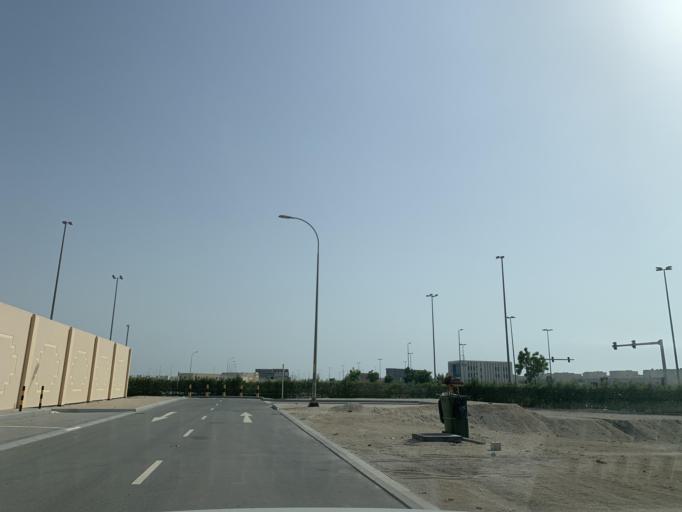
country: BH
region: Muharraq
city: Al Muharraq
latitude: 26.3101
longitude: 50.6321
